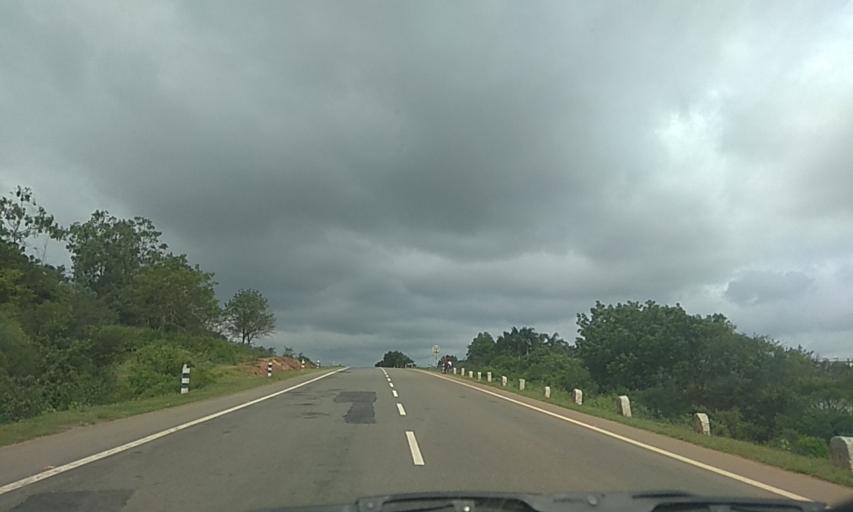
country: IN
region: Karnataka
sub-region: Dharwad
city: Hubli
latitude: 15.3416
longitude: 75.0815
